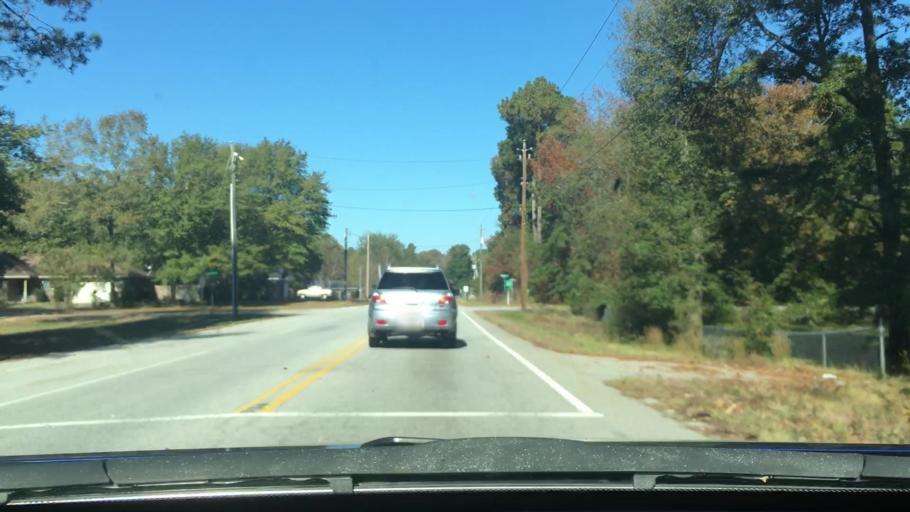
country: US
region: South Carolina
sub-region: Sumter County
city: South Sumter
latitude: 33.8914
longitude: -80.3669
